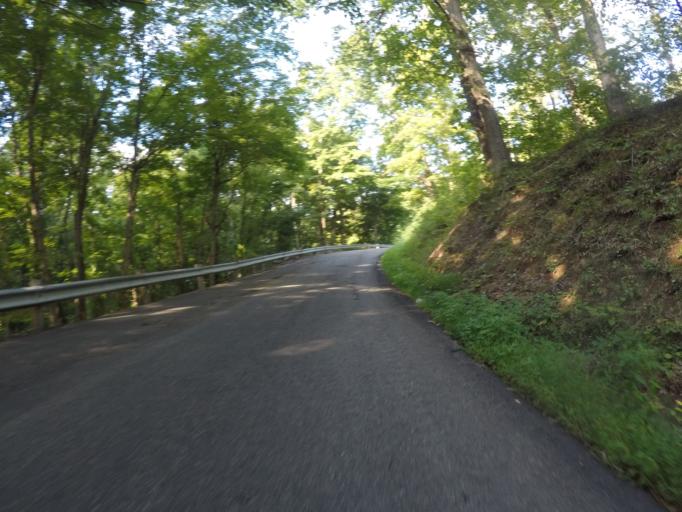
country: US
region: West Virginia
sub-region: Cabell County
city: Huntington
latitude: 38.4557
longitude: -82.4617
